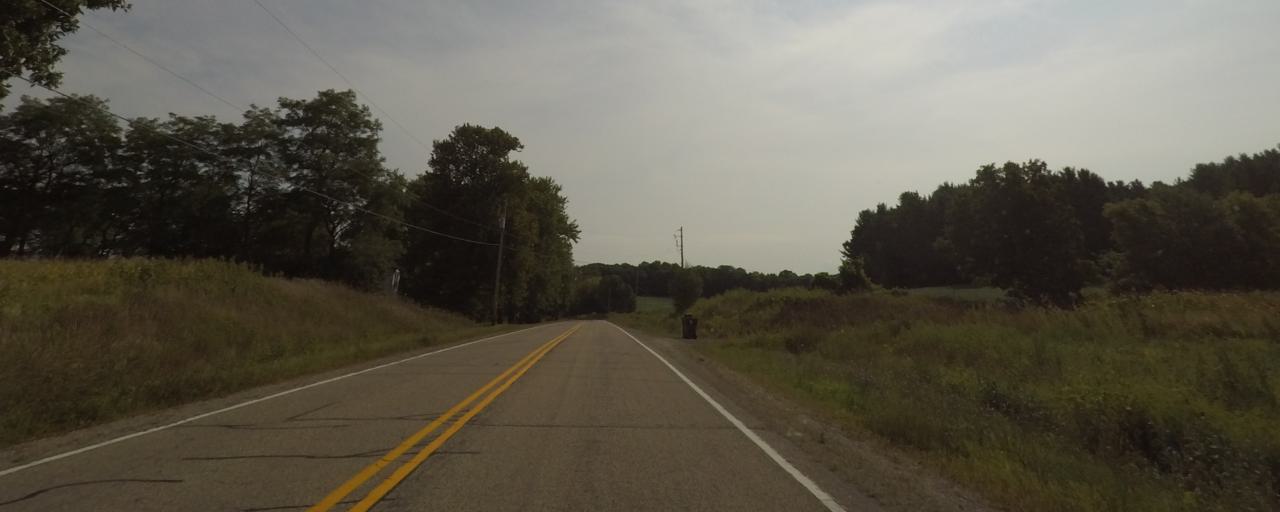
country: US
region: Wisconsin
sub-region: Jefferson County
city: Lake Koshkonong
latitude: 42.9713
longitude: -88.9048
